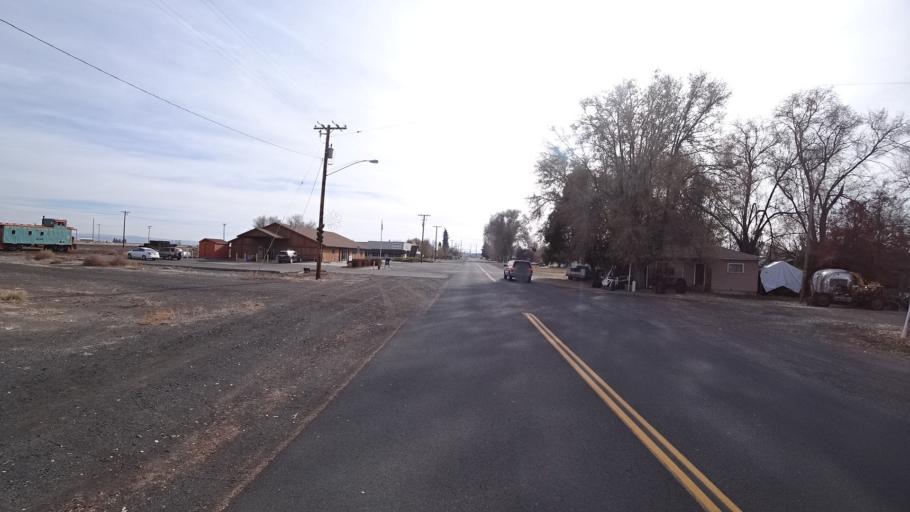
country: US
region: California
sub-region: Siskiyou County
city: Tulelake
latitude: 41.9563
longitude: -121.4748
